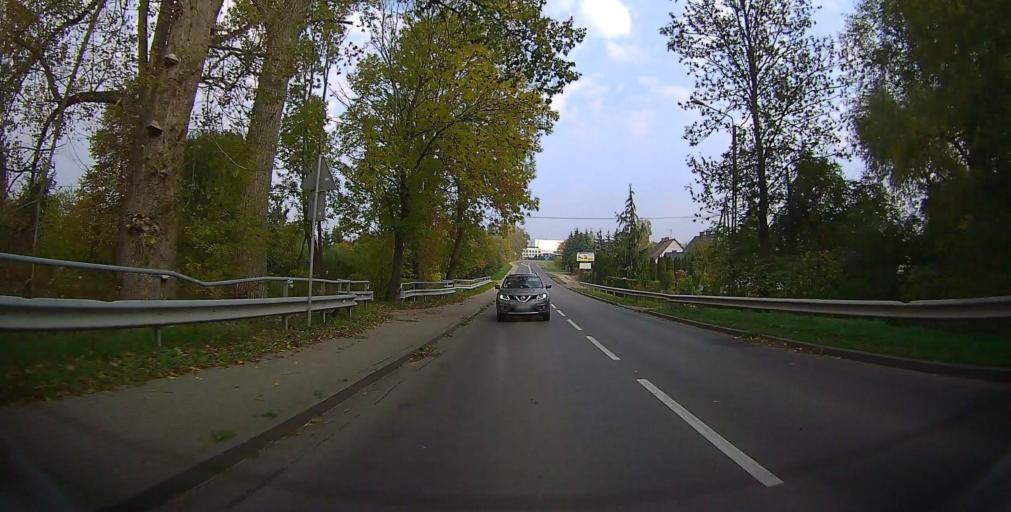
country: PL
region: Masovian Voivodeship
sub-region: Powiat grojecki
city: Belsk Duzy
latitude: 51.8139
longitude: 20.7967
